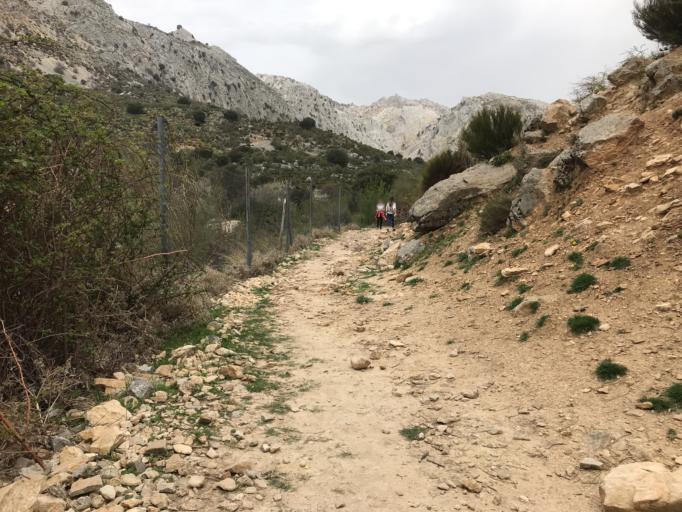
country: ES
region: Andalusia
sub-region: Provincia de Granada
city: Castril
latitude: 37.8954
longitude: -2.7476
